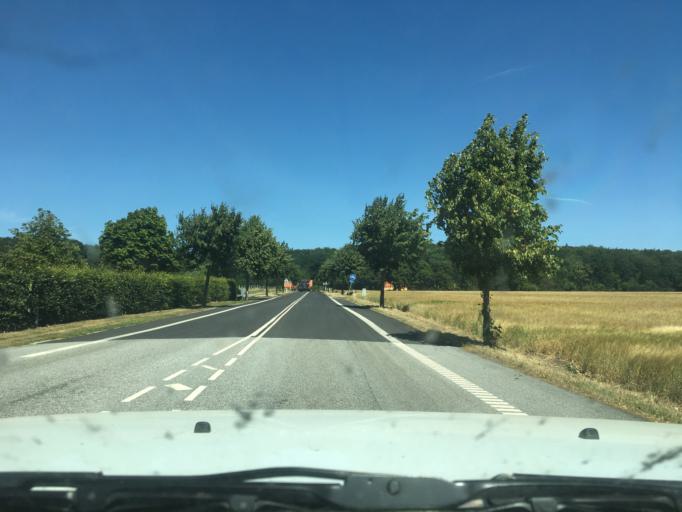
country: DK
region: Central Jutland
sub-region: Favrskov Kommune
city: Ulstrup
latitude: 56.3963
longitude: 9.7938
